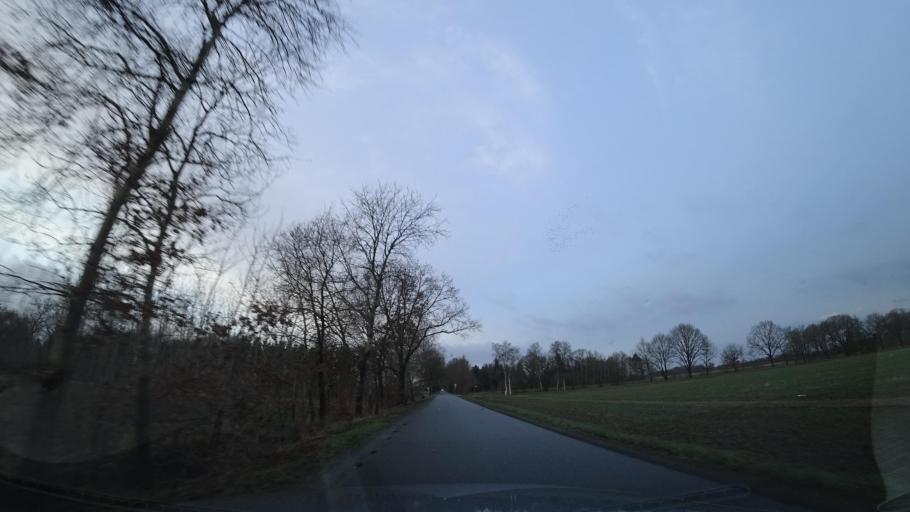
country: DE
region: Lower Saxony
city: Hatten
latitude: 53.0509
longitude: 8.2950
